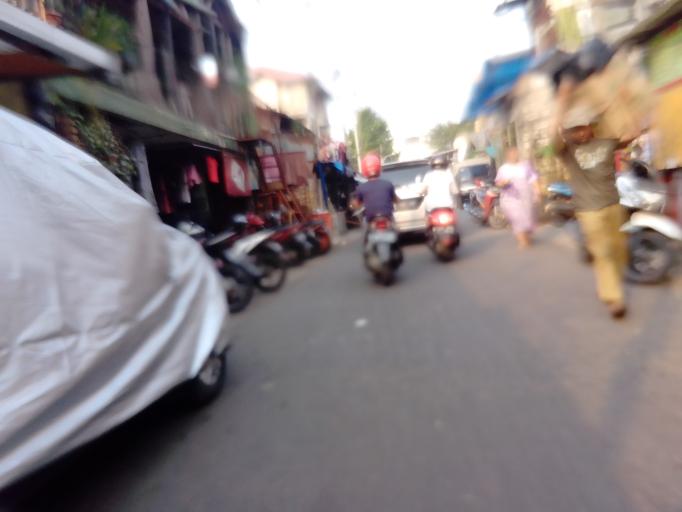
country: ID
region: Jakarta Raya
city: Jakarta
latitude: -6.1911
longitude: 106.8118
